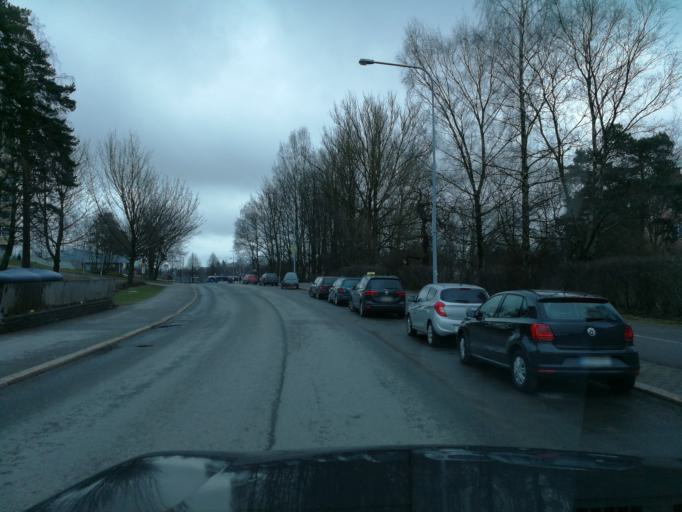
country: FI
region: Uusimaa
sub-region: Helsinki
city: Helsinki
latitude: 60.2170
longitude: 24.9650
